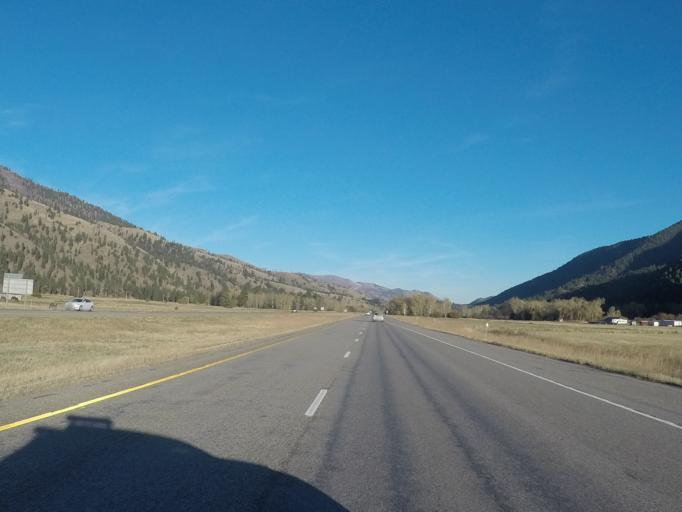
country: US
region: Montana
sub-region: Missoula County
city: Clinton
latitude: 46.7271
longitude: -113.6654
